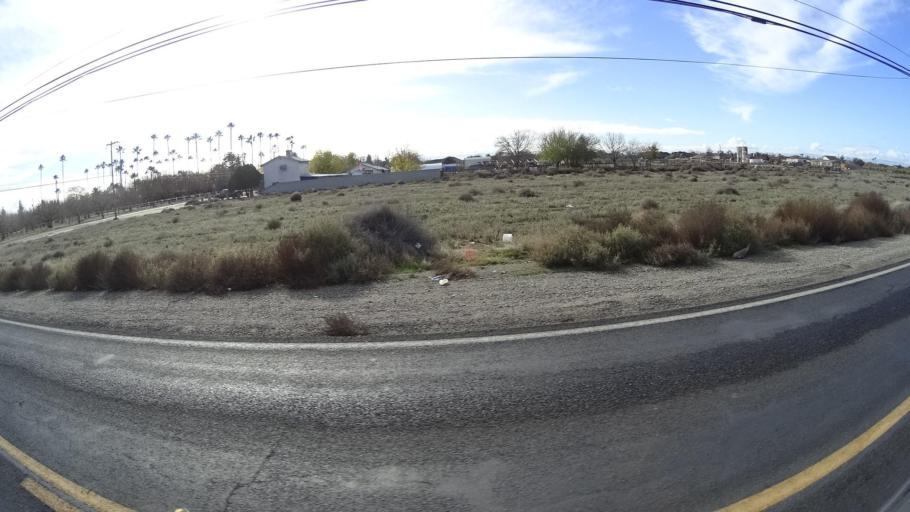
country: US
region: California
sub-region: Kern County
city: Rosedale
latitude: 35.3835
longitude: -119.1903
